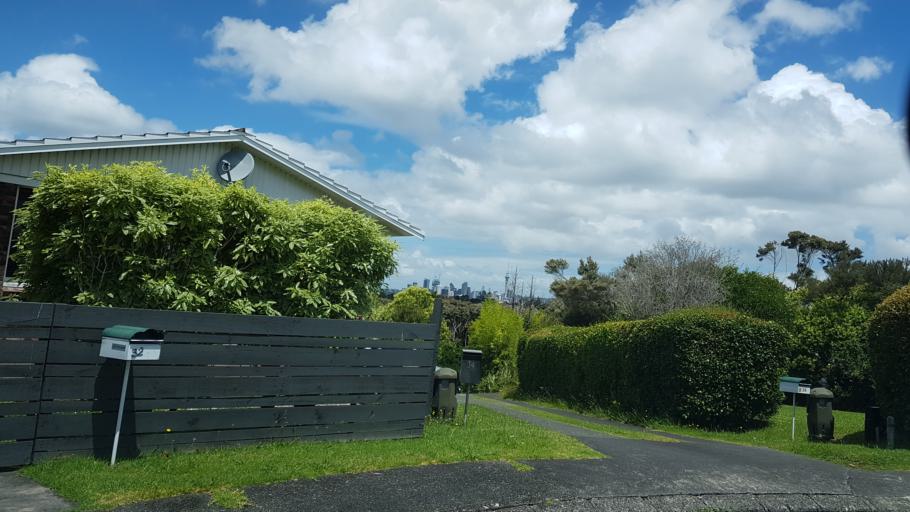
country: NZ
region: Auckland
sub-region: Auckland
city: North Shore
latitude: -36.8047
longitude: 174.7429
